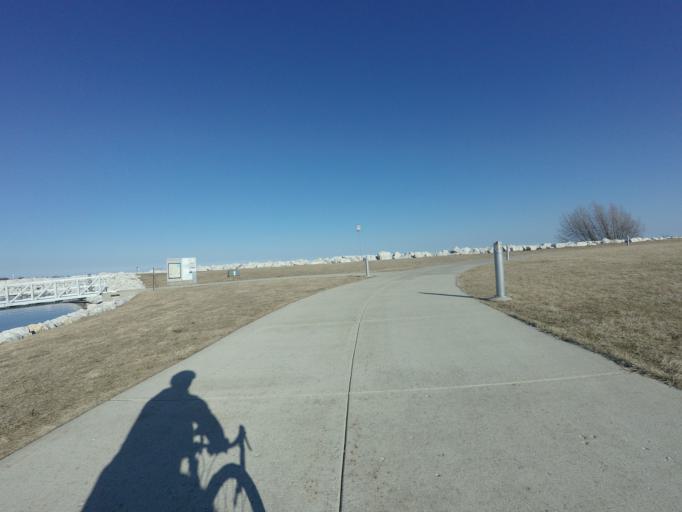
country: US
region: Wisconsin
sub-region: Milwaukee County
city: Milwaukee
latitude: 43.0341
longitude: -87.8955
